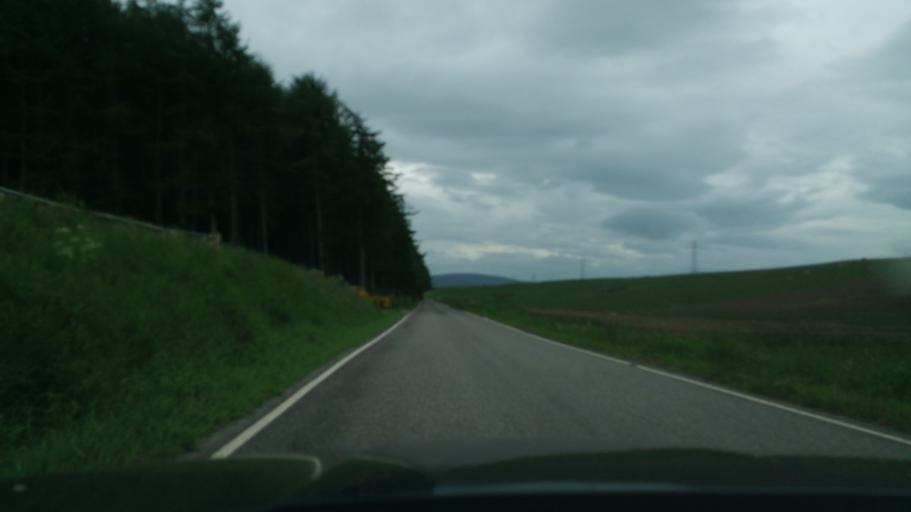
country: GB
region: Scotland
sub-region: Moray
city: Cullen
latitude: 57.5999
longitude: -2.8545
